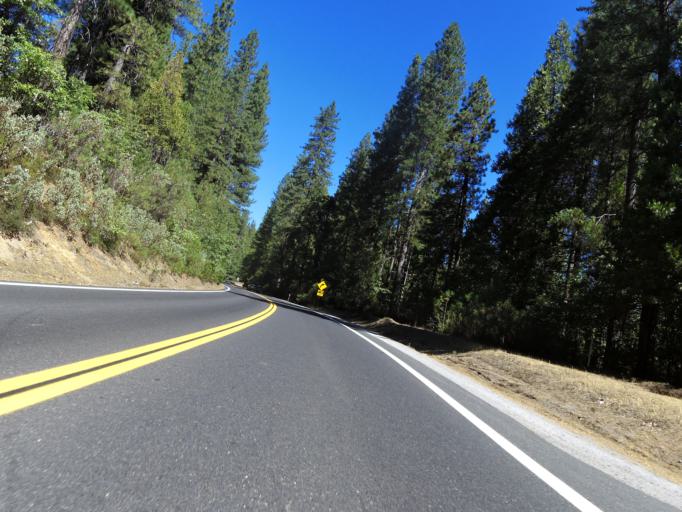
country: US
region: California
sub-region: Calaveras County
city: Arnold
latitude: 38.2228
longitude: -120.3689
